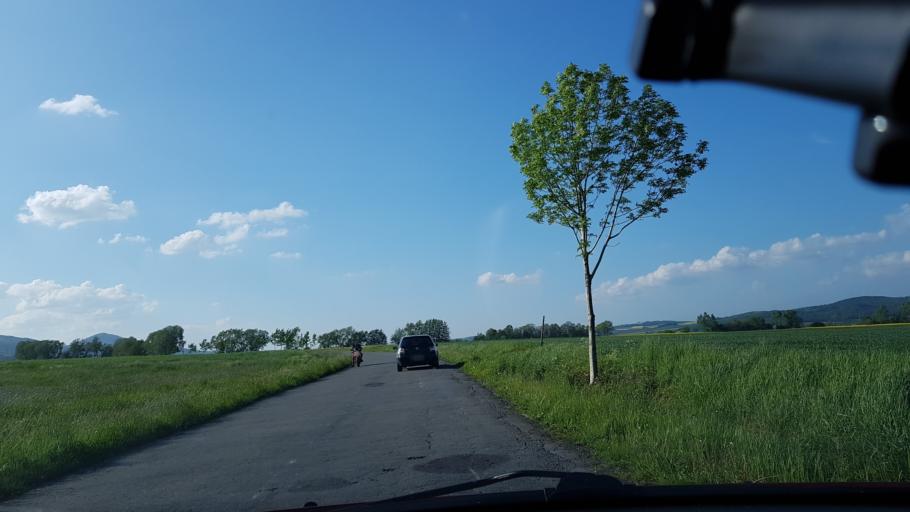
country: PL
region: Lower Silesian Voivodeship
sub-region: Powiat zabkowicki
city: Budzow
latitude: 50.5775
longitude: 16.6777
